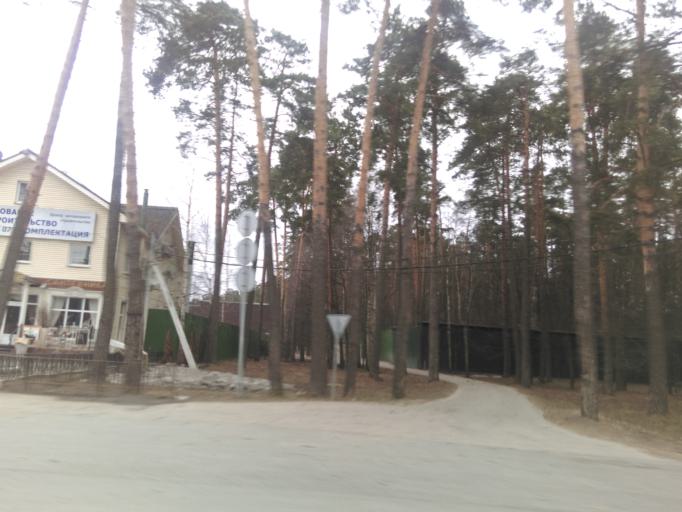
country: RU
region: Moskovskaya
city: Gorki Vtoryye
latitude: 55.7242
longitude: 37.1592
